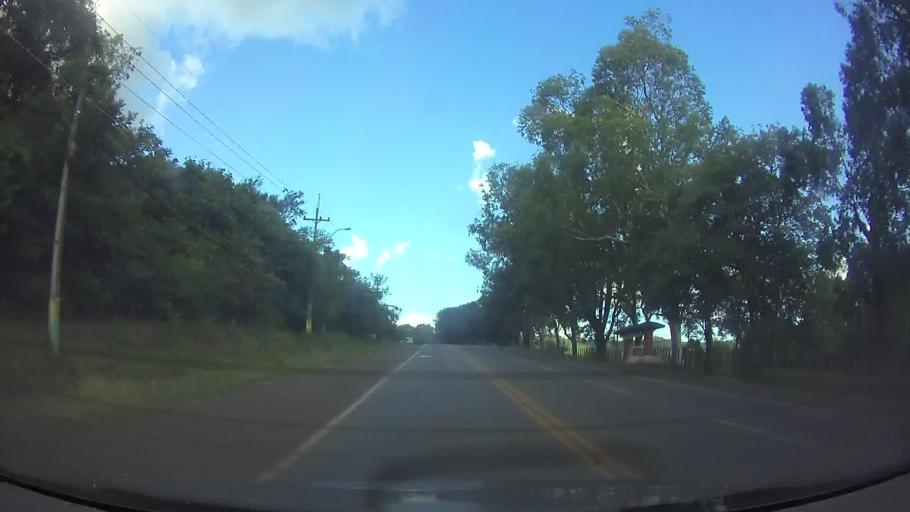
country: PY
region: Cordillera
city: Caacupe
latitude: -25.3865
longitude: -57.1199
